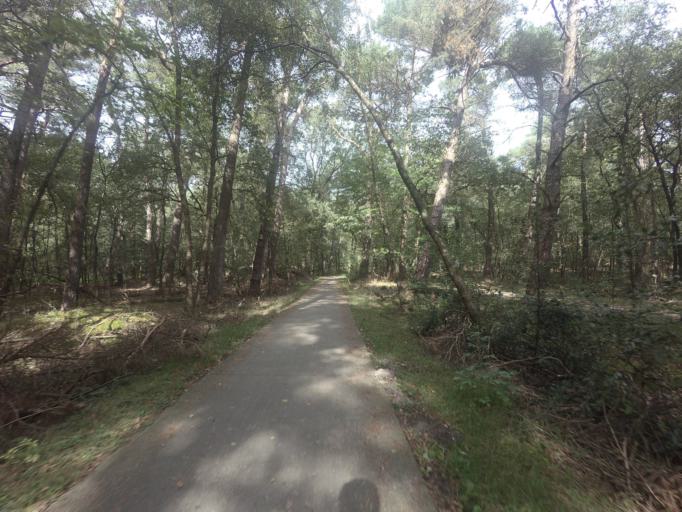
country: NL
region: Drenthe
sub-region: Gemeente Westerveld
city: Dwingeloo
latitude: 52.8741
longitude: 6.2829
